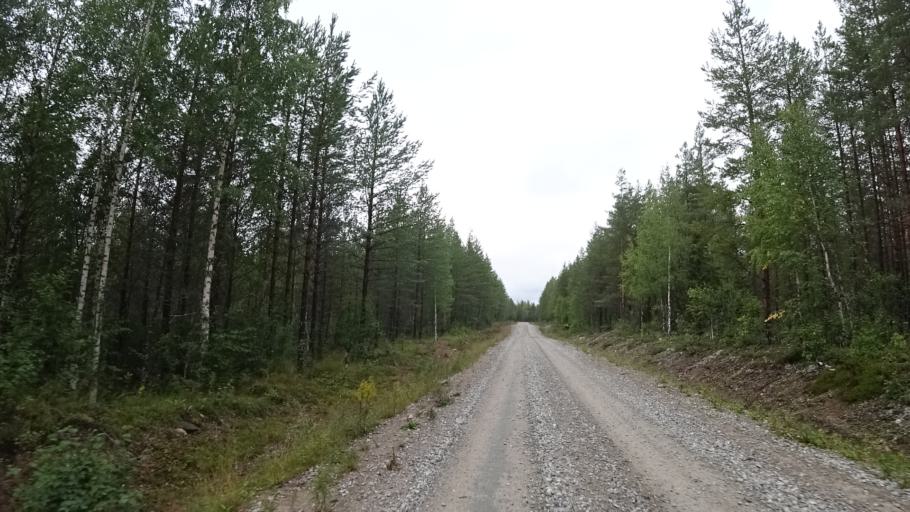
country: FI
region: North Karelia
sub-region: Pielisen Karjala
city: Lieksa
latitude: 63.4682
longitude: 30.2832
